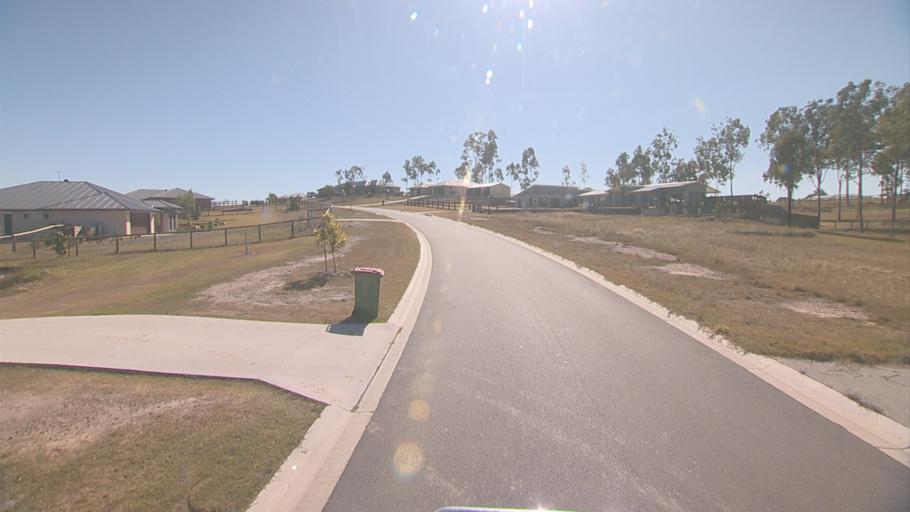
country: AU
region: Queensland
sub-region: Logan
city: Cedar Vale
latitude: -27.8649
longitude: 153.0438
